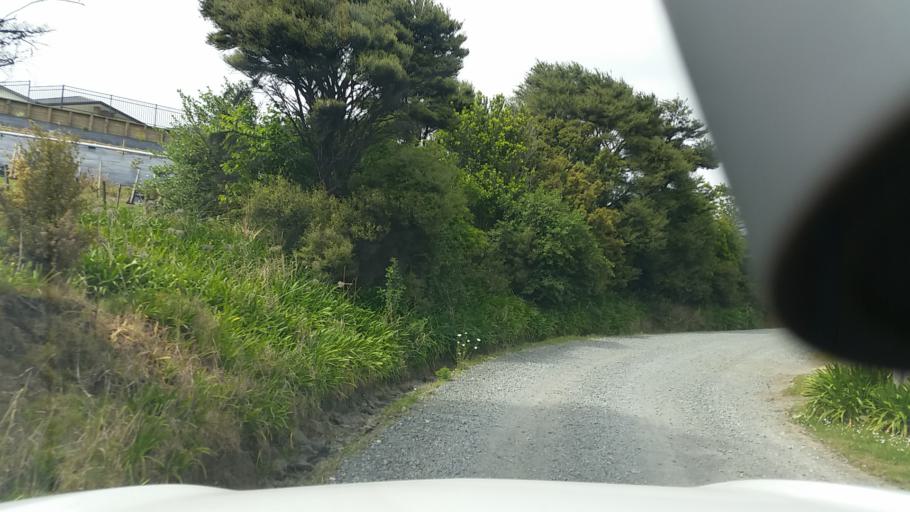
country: NZ
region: Auckland
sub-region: Auckland
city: Muriwai Beach
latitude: -36.8463
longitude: 174.5229
